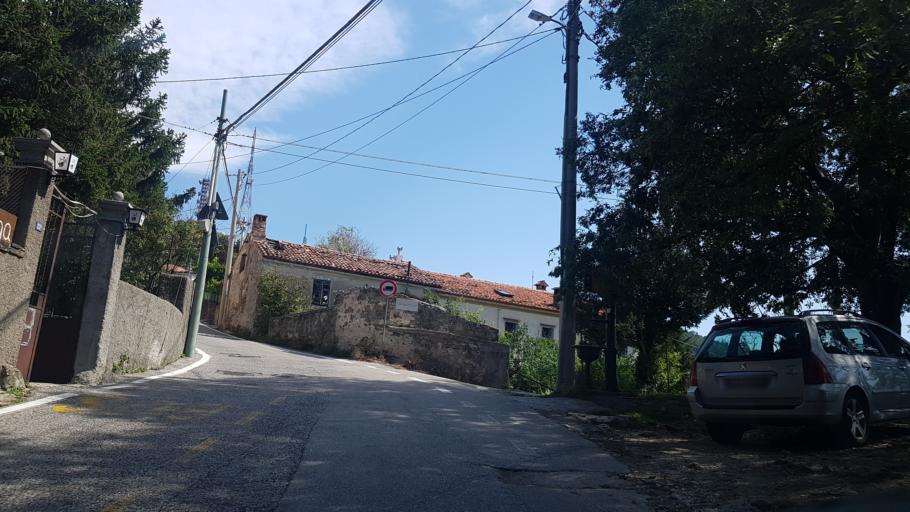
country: IT
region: Friuli Venezia Giulia
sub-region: Provincia di Trieste
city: Villa Opicina
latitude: 45.6700
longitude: 13.7941
